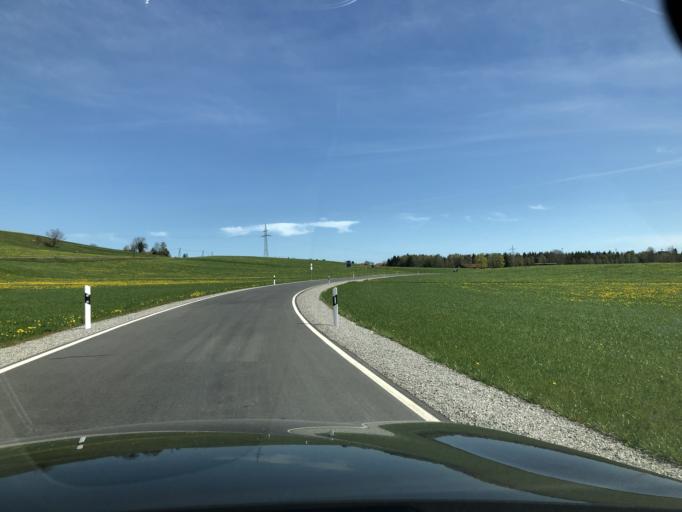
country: DE
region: Bavaria
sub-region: Swabia
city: Seeg
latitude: 47.6447
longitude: 10.6134
